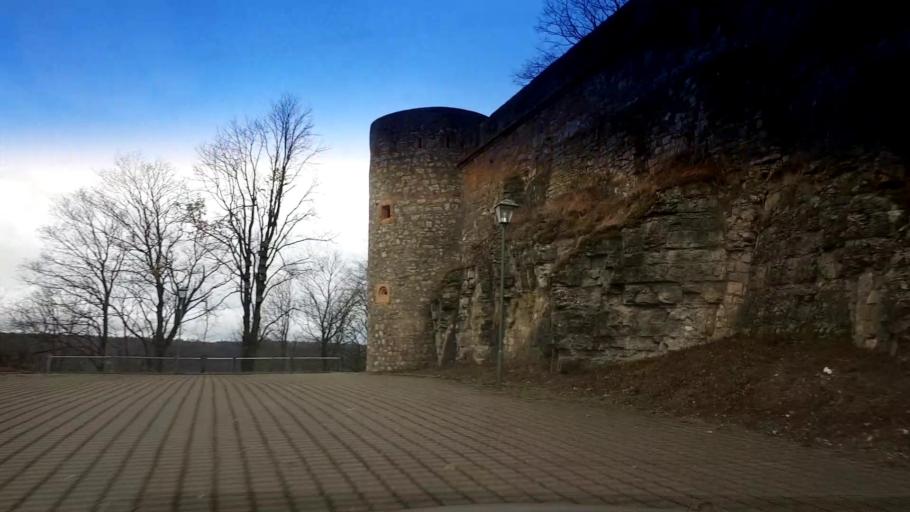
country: DE
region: Bavaria
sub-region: Upper Franconia
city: Schesslitz
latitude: 49.9552
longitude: 11.0500
